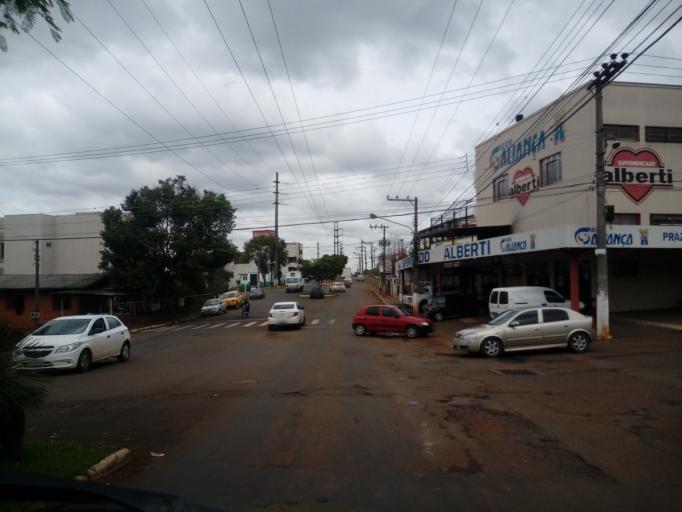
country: BR
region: Santa Catarina
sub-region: Chapeco
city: Chapeco
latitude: -27.0790
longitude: -52.6132
